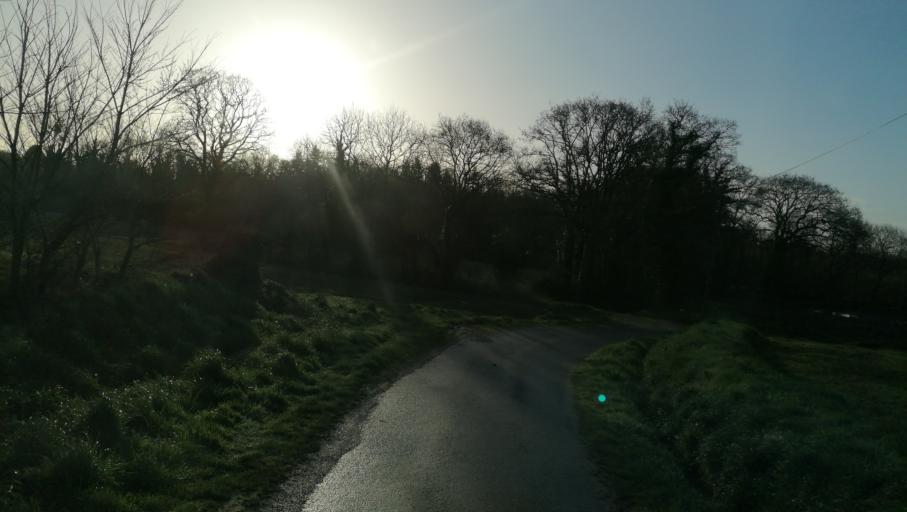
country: FR
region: Brittany
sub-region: Departement des Cotes-d'Armor
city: Plouha
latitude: 48.6656
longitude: -2.9143
